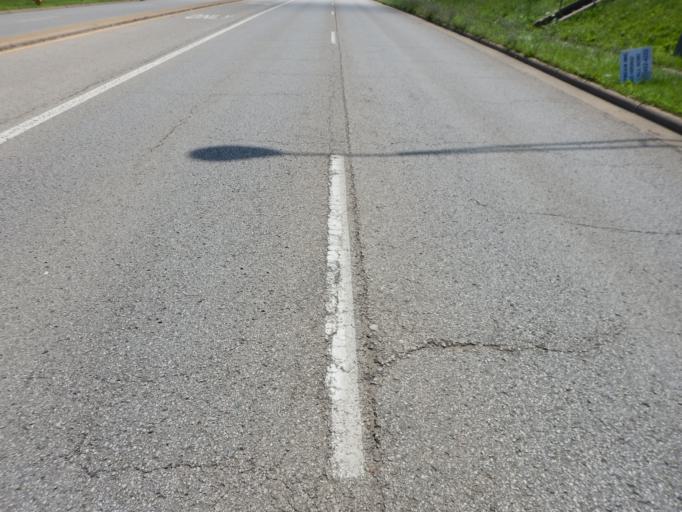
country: US
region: Ohio
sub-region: Muskingum County
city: Zanesville
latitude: 39.9531
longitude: -82.0094
